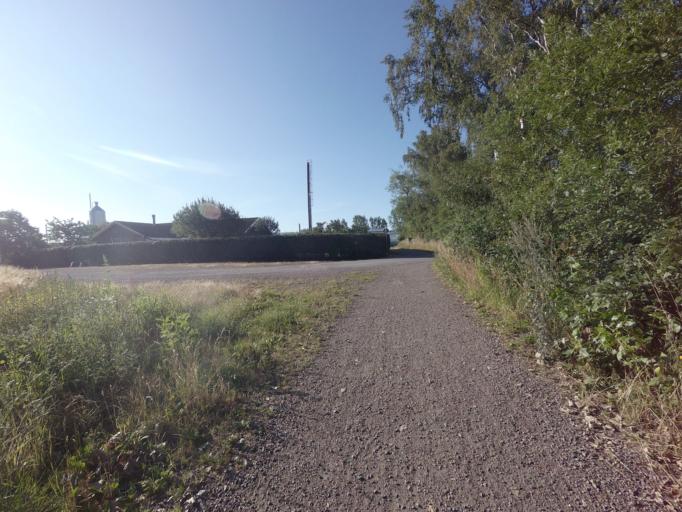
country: SE
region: Skane
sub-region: Hoganas Kommun
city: Hoganas
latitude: 56.1448
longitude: 12.5883
